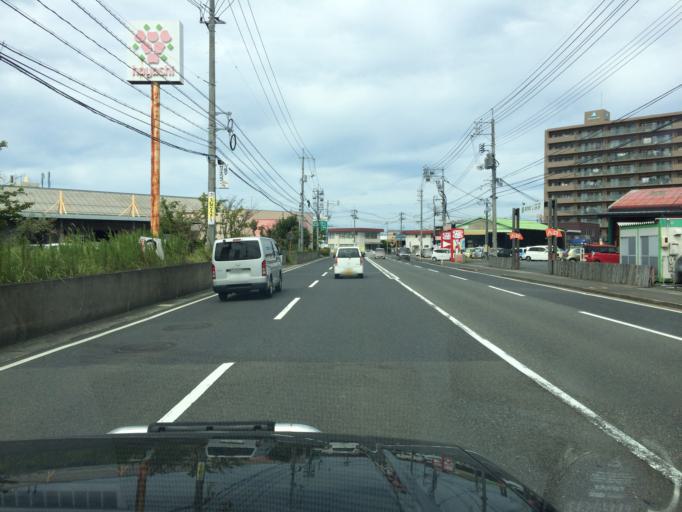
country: JP
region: Tottori
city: Tottori
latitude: 35.5116
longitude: 134.1929
